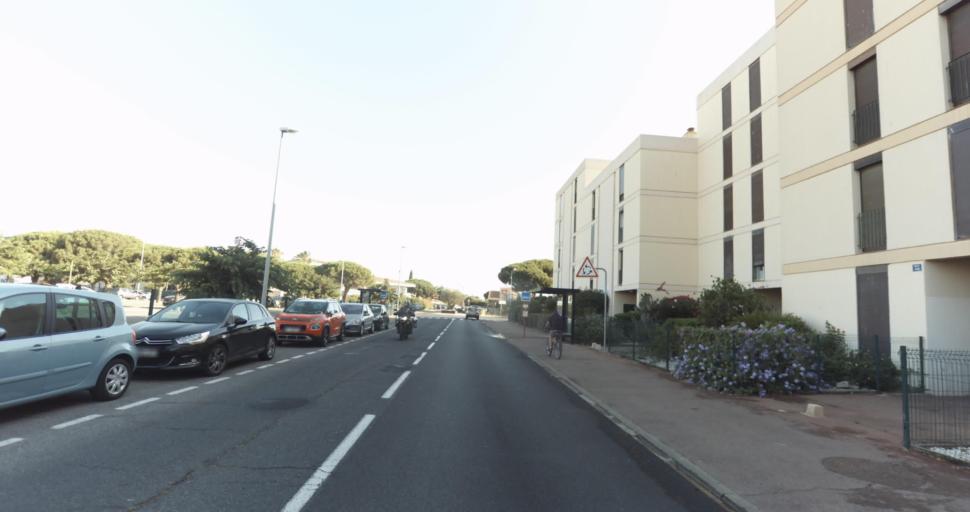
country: FR
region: Languedoc-Roussillon
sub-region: Departement des Pyrenees-Orientales
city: Saint-Cyprien-Plage
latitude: 42.6248
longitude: 3.0322
